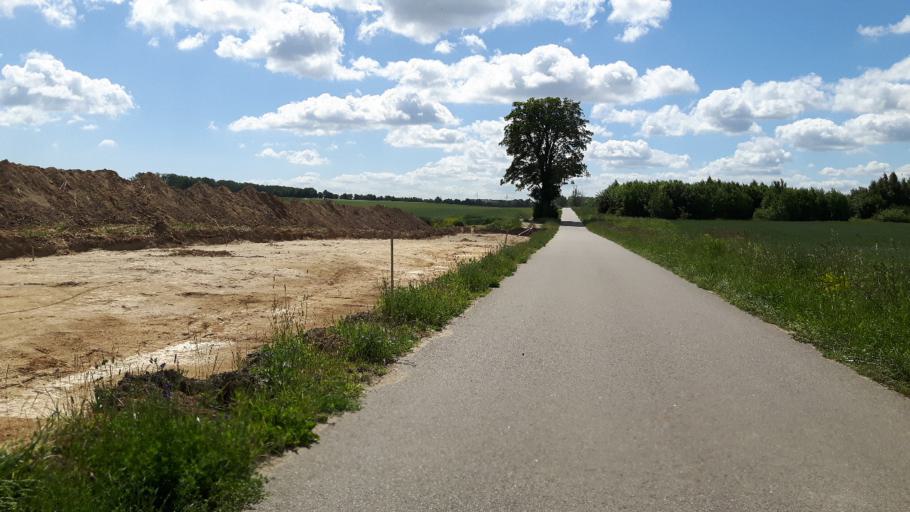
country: PL
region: Pomeranian Voivodeship
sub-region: Gdynia
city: Pogorze
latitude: 54.5741
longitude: 18.4976
